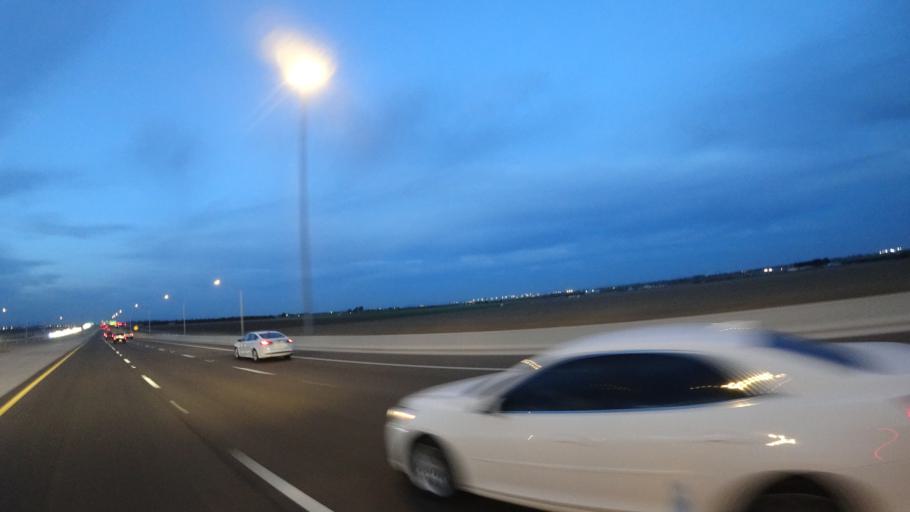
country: US
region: Arizona
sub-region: Maricopa County
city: Citrus Park
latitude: 33.5099
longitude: -112.4184
